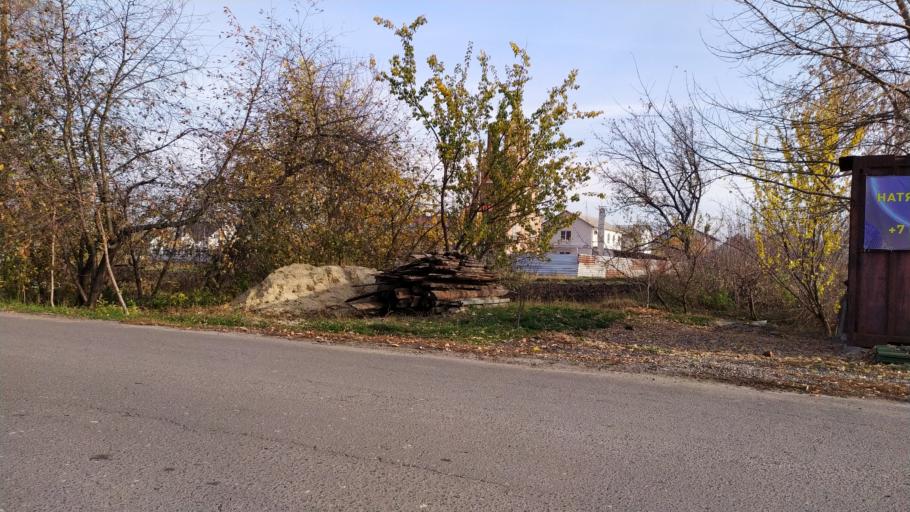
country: RU
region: Kursk
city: Kursk
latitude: 51.6419
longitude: 36.1492
